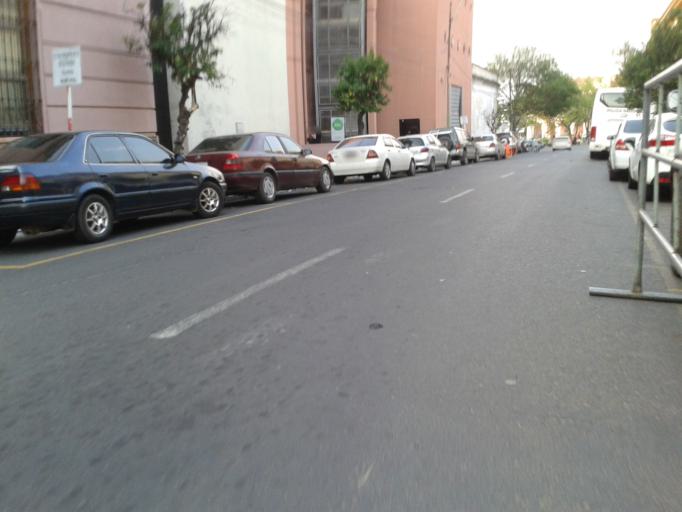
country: PY
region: Asuncion
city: Asuncion
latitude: -25.2817
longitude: -57.6348
